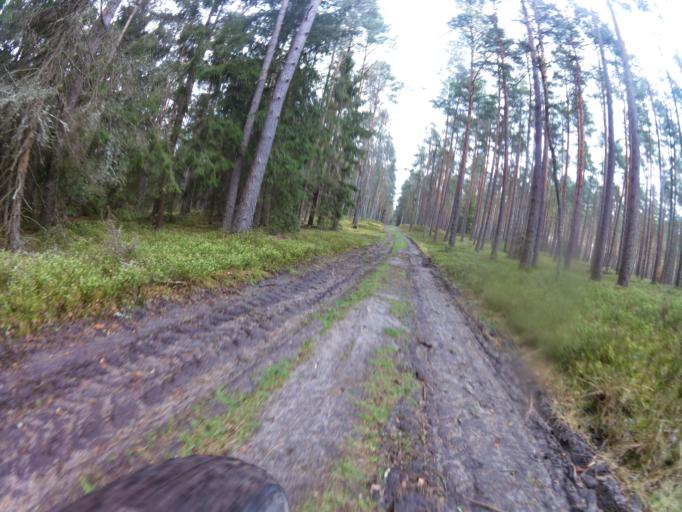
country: PL
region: Pomeranian Voivodeship
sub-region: Powiat slupski
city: Kepice
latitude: 54.2318
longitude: 16.7756
